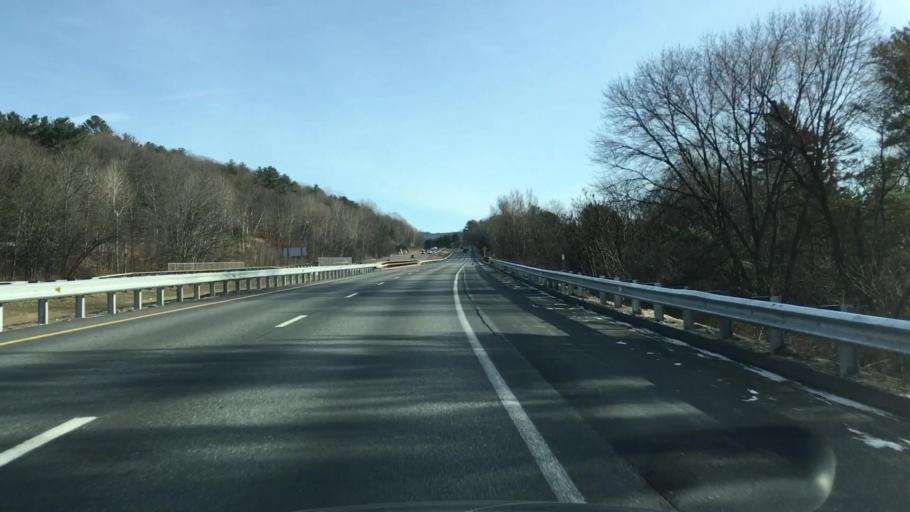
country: US
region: New Hampshire
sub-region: Grafton County
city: Lebanon
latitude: 43.6460
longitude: -72.2351
